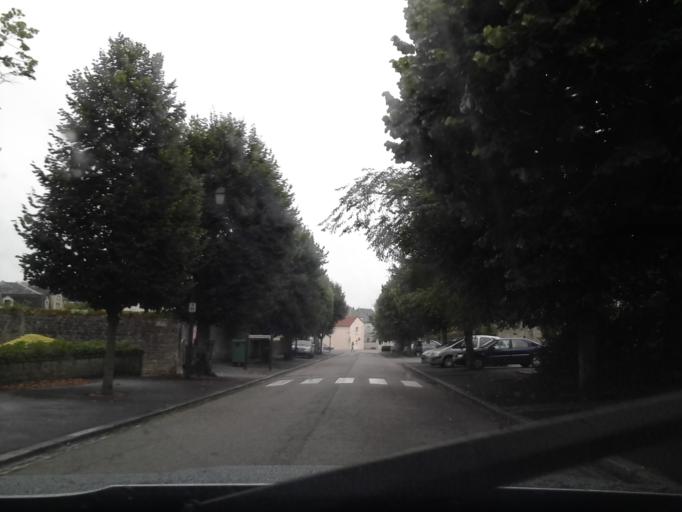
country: FR
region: Lower Normandy
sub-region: Departement de la Manche
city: Carentan
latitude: 49.3059
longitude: -1.2427
